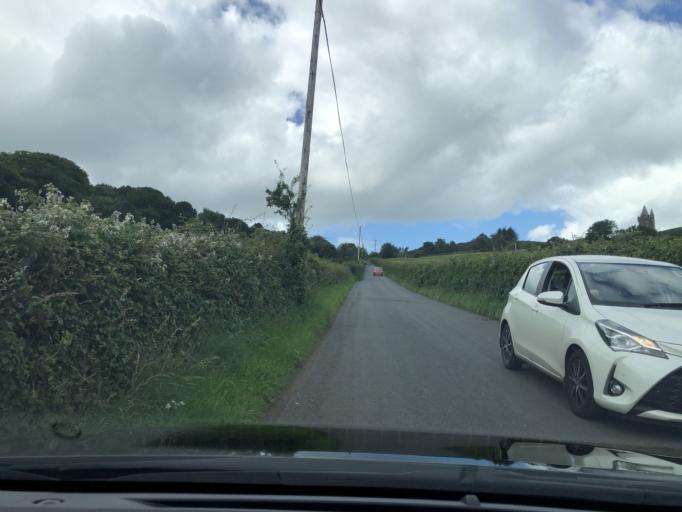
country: GB
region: Northern Ireland
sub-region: Ards District
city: Newtownards
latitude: 54.5751
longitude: -5.7167
